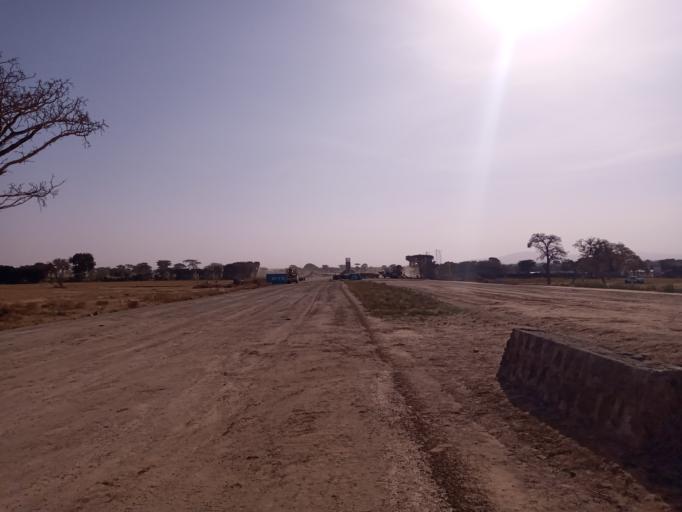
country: ET
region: Oromiya
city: Shashemene
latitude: 7.3067
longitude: 38.6201
